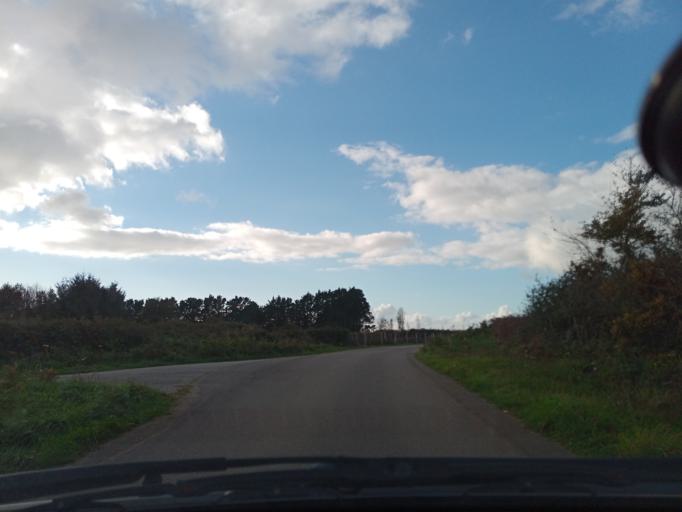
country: FR
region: Brittany
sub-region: Departement du Finistere
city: Plouhinec
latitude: 48.0178
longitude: -4.4969
